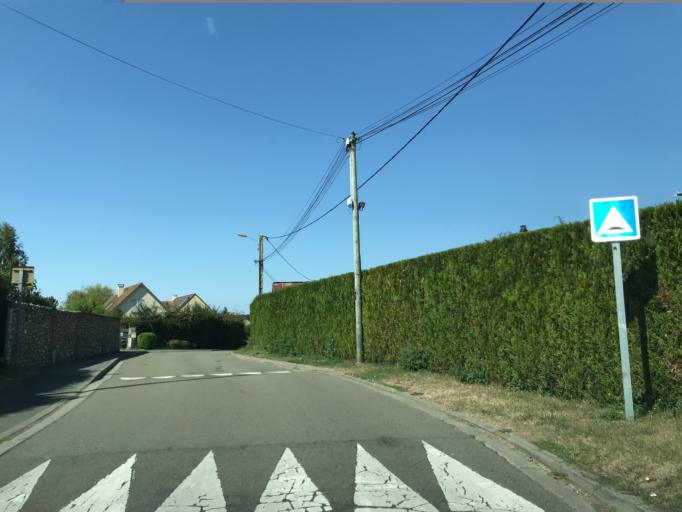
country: FR
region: Haute-Normandie
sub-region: Departement de l'Eure
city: Heudreville-sur-Eure
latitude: 49.0964
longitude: 1.2046
